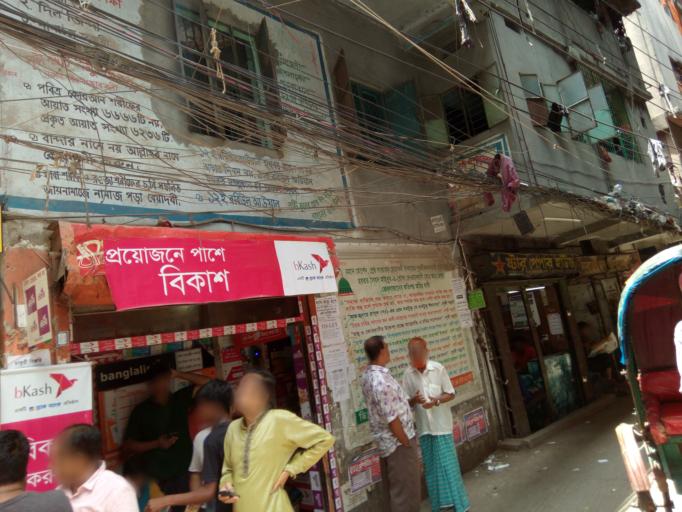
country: BD
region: Dhaka
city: Paltan
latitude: 23.7313
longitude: 90.4163
